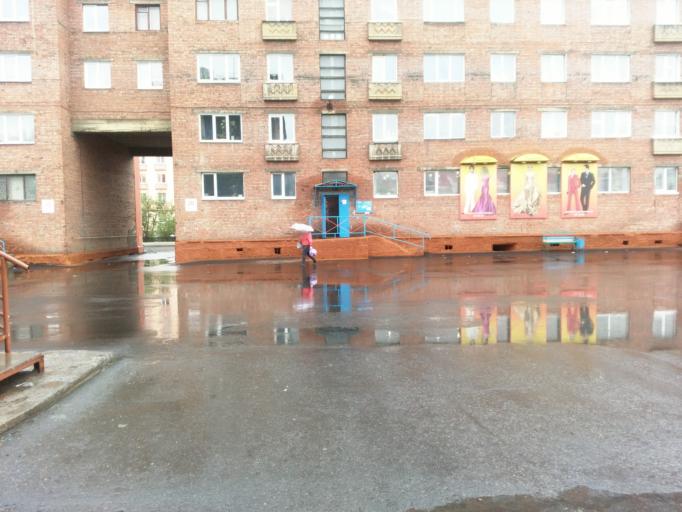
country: RU
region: Krasnoyarskiy
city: Norilsk
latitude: 69.3514
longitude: 88.1988
